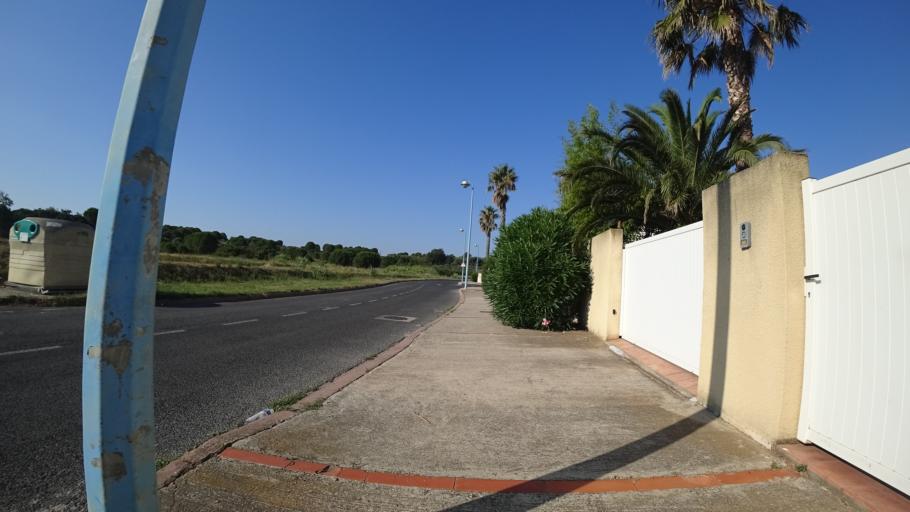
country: FR
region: Languedoc-Roussillon
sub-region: Departement des Pyrenees-Orientales
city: Canet-en-Roussillon
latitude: 42.6995
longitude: 2.9957
